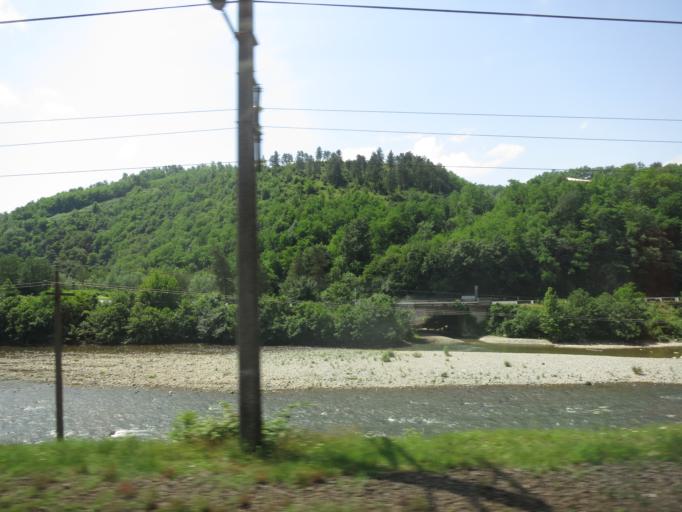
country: GE
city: Shorapani
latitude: 42.0946
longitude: 43.0898
